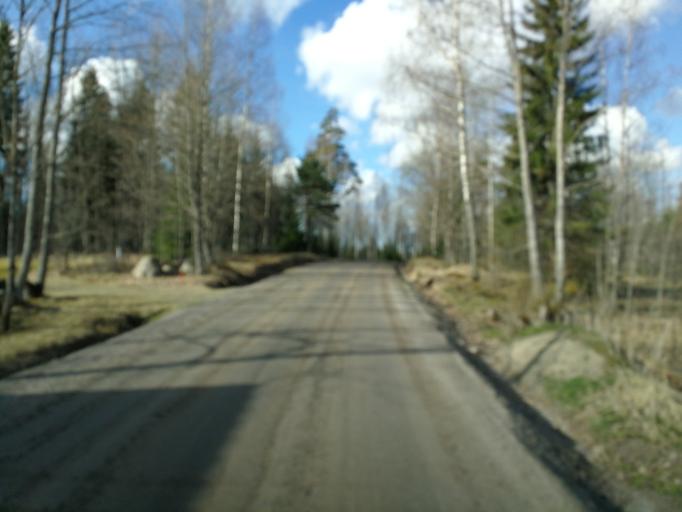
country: FI
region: Uusimaa
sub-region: Raaseporin
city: Inga
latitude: 60.1235
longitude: 24.0493
